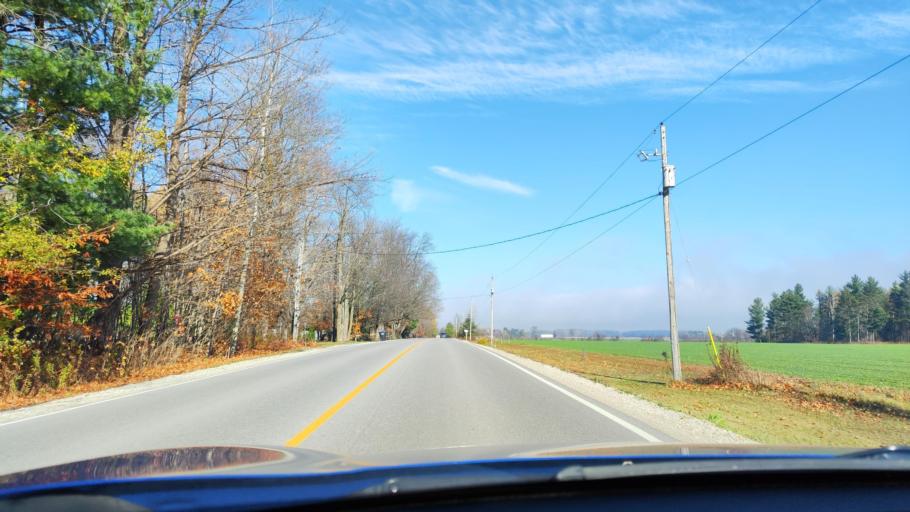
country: CA
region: Ontario
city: Wasaga Beach
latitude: 44.4114
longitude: -80.0603
